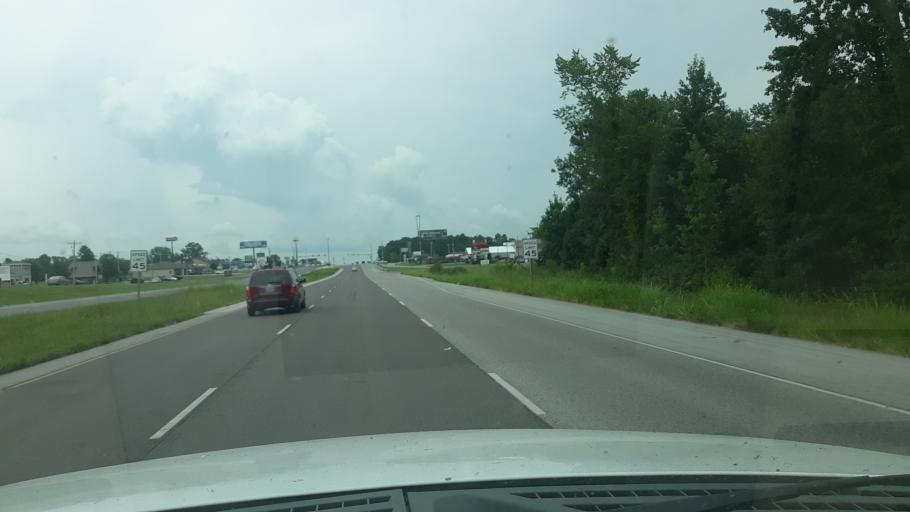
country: US
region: Illinois
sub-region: Williamson County
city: Carterville
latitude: 37.7449
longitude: -89.0832
